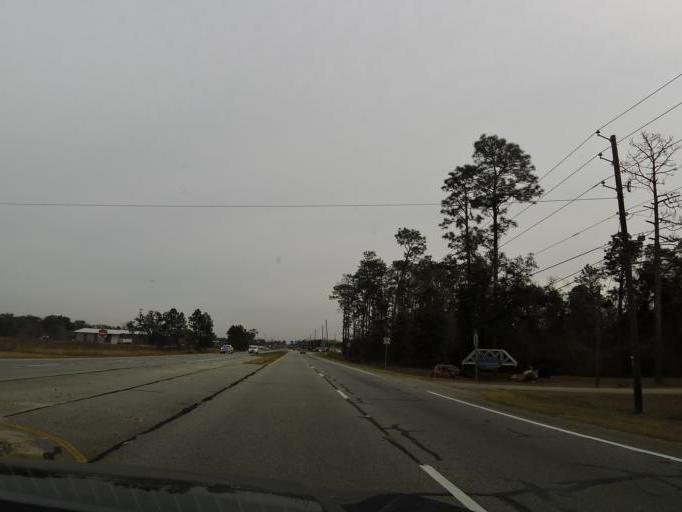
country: US
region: Georgia
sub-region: Decatur County
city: Bainbridge
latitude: 30.9238
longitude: -84.6121
